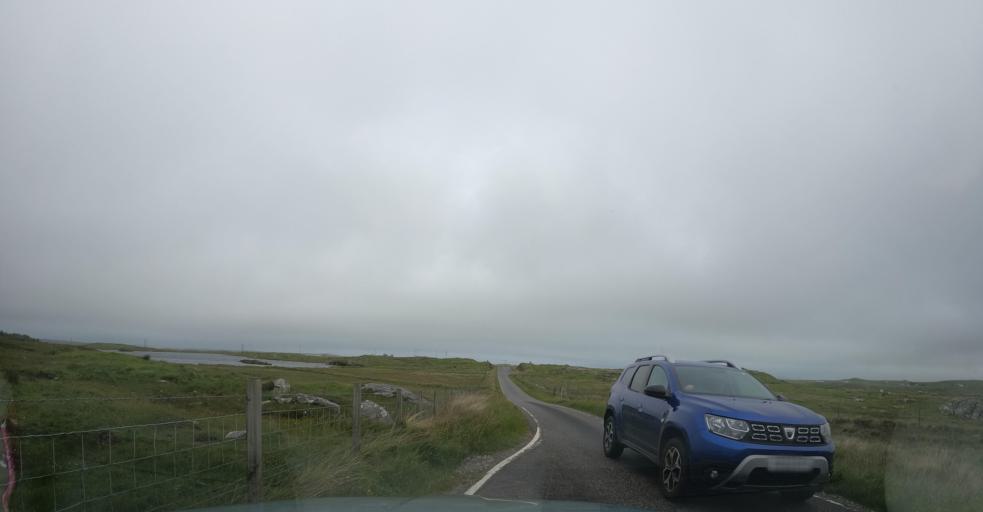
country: GB
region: Scotland
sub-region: Eilean Siar
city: Isle of North Uist
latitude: 57.6490
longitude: -7.2449
